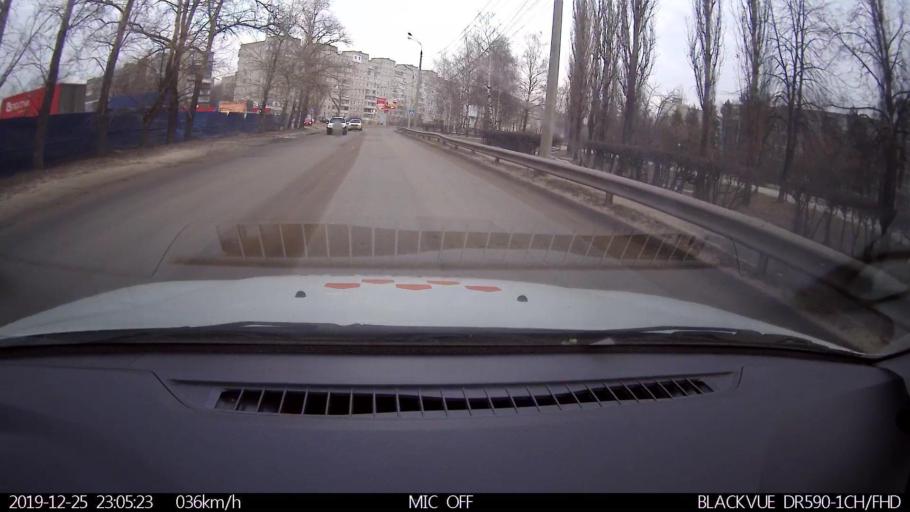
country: RU
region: Nizjnij Novgorod
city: Gorbatovka
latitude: 56.3598
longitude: 43.8059
